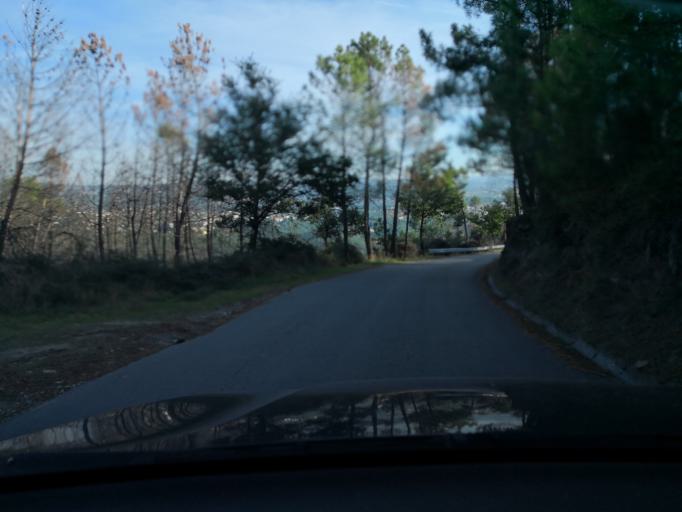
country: PT
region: Vila Real
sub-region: Vila Real
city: Vila Real
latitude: 41.3374
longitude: -7.7450
